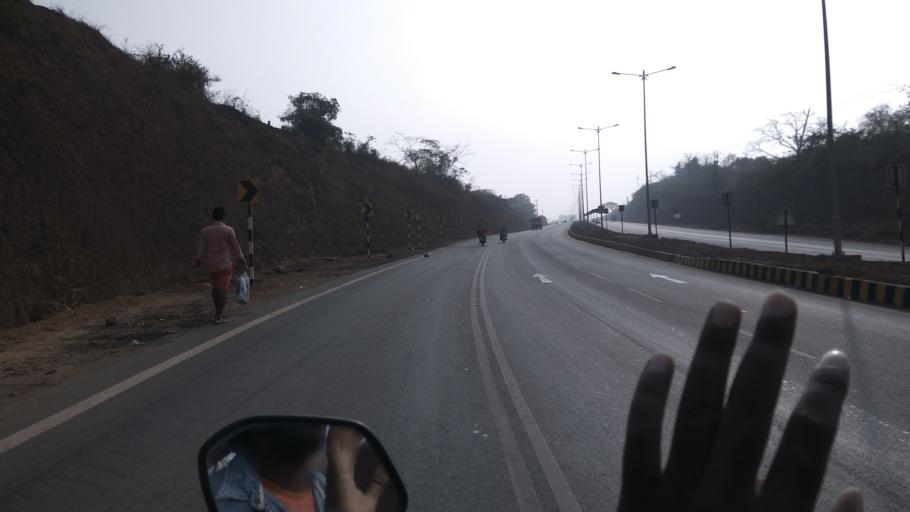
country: IN
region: Goa
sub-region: North Goa
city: Bambolim
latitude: 15.5002
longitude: 73.8654
